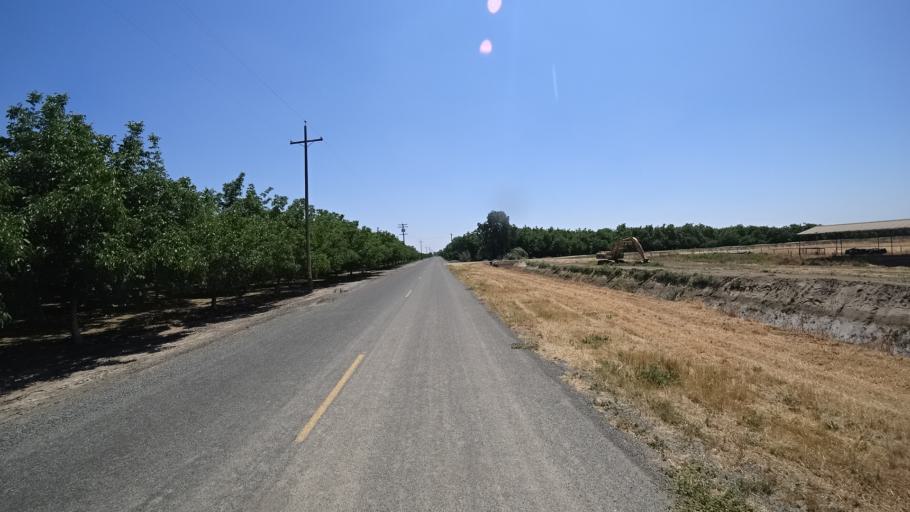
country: US
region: California
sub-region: Fresno County
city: Laton
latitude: 36.4143
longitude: -119.6955
